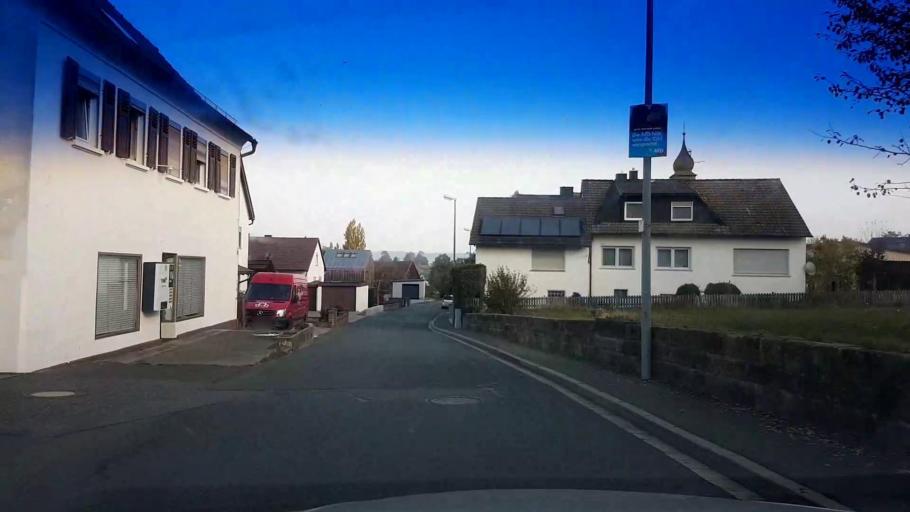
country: DE
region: Bavaria
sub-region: Upper Franconia
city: Altenkunstadt
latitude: 50.1065
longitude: 11.2554
